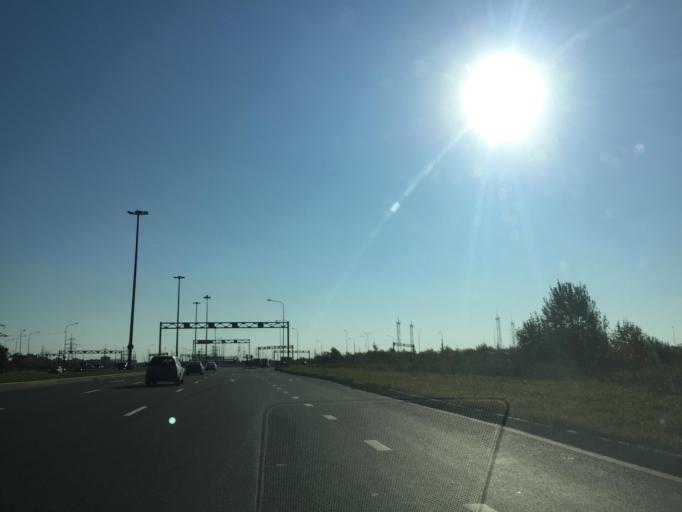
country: RU
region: St.-Petersburg
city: Metallostroy
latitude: 59.7504
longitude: 30.5282
